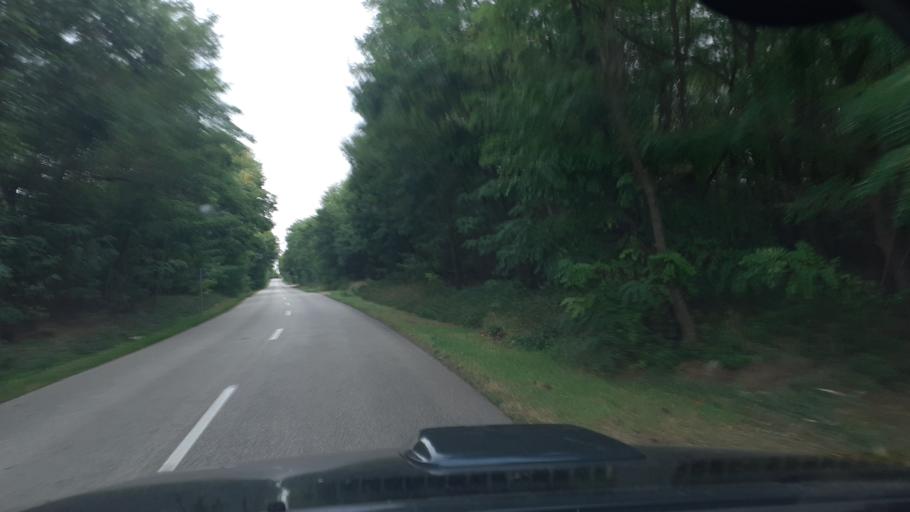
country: HU
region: Fejer
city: Baracs
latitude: 46.8444
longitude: 18.8902
